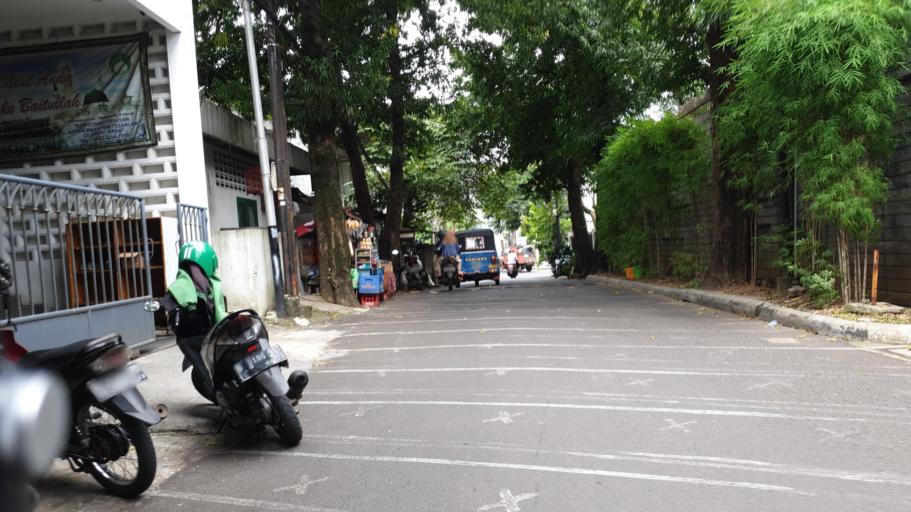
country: ID
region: Banten
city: South Tangerang
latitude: -6.2874
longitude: 106.7936
